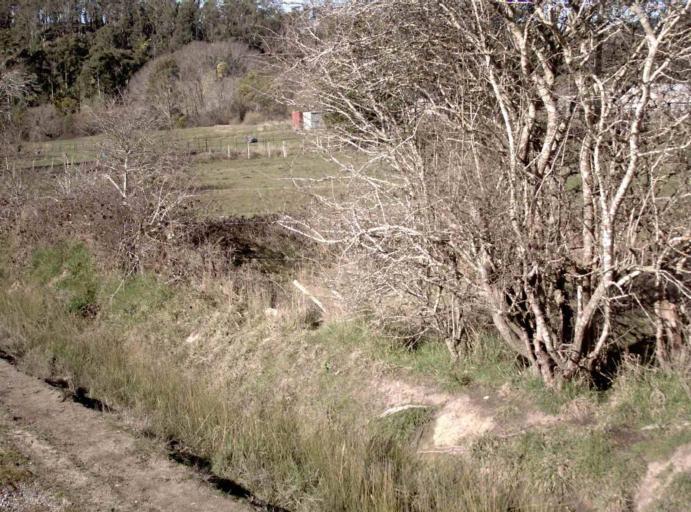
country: AU
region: Tasmania
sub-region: Launceston
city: Mayfield
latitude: -41.2555
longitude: 147.1530
